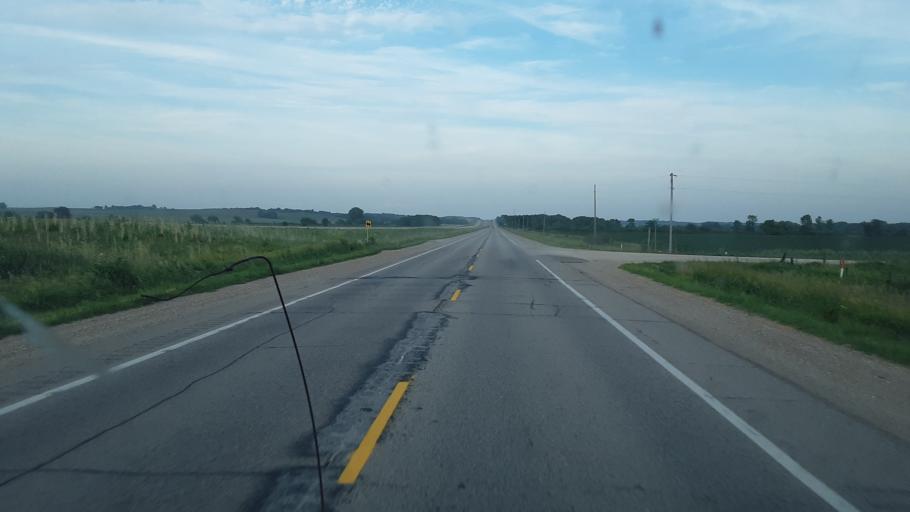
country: US
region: Iowa
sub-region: Tama County
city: Tama
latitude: 41.9638
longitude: -92.4892
